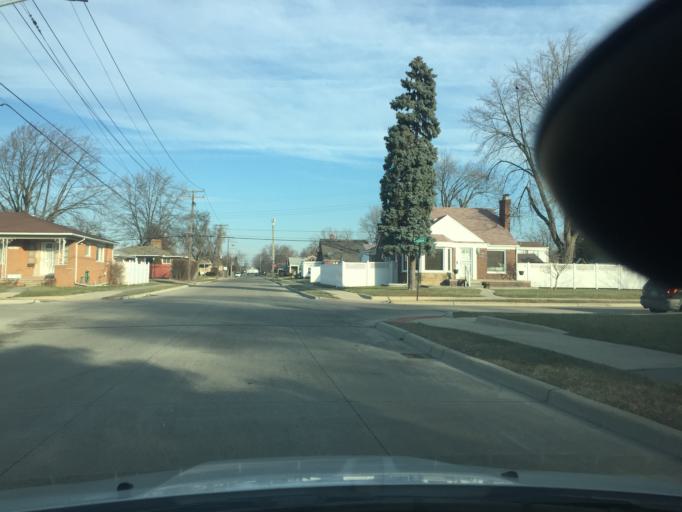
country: US
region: Michigan
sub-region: Macomb County
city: Eastpointe
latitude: 42.4515
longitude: -82.9611
